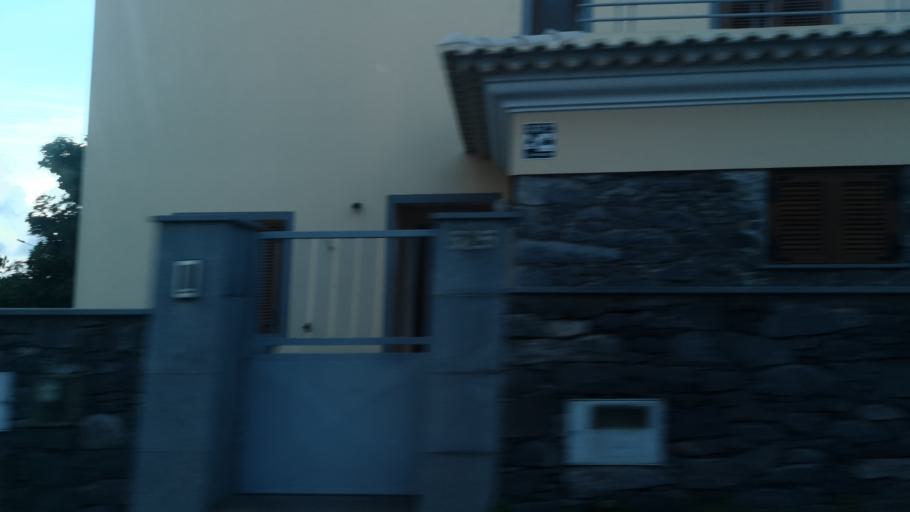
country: PT
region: Madeira
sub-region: Santa Cruz
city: Camacha
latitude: 32.6801
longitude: -16.8266
